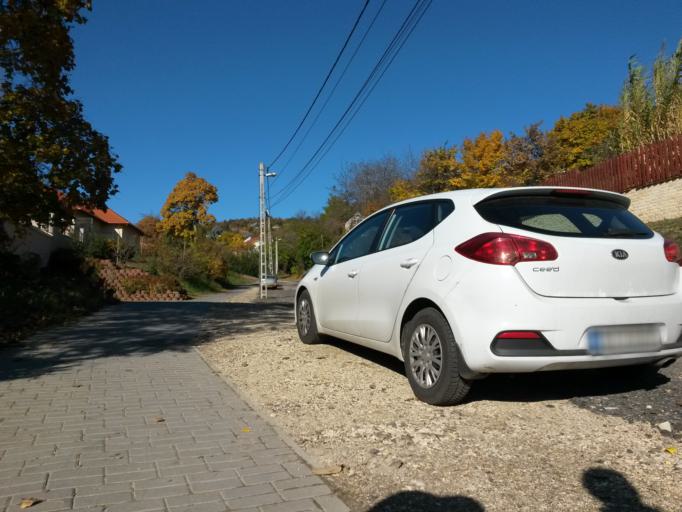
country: HU
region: Pest
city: Budaors
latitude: 47.4804
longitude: 18.9808
